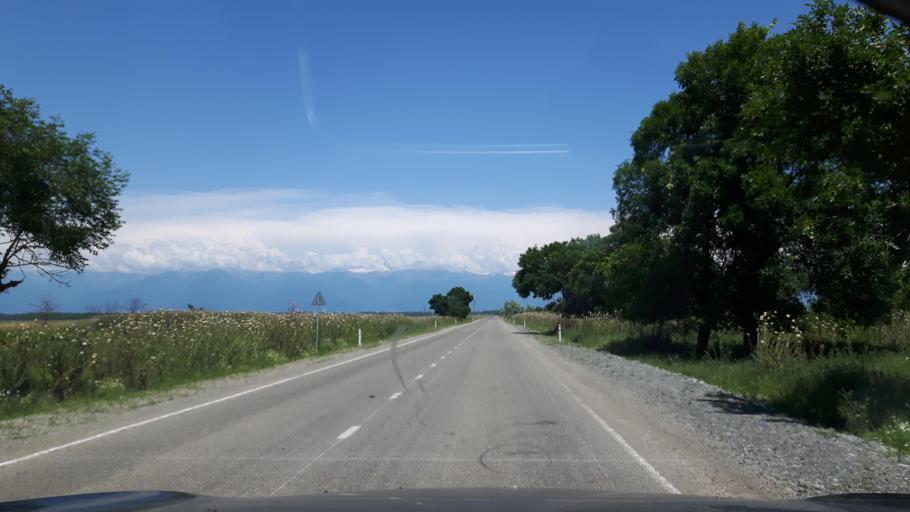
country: GE
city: Tsnori
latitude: 41.6387
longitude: 46.0348
